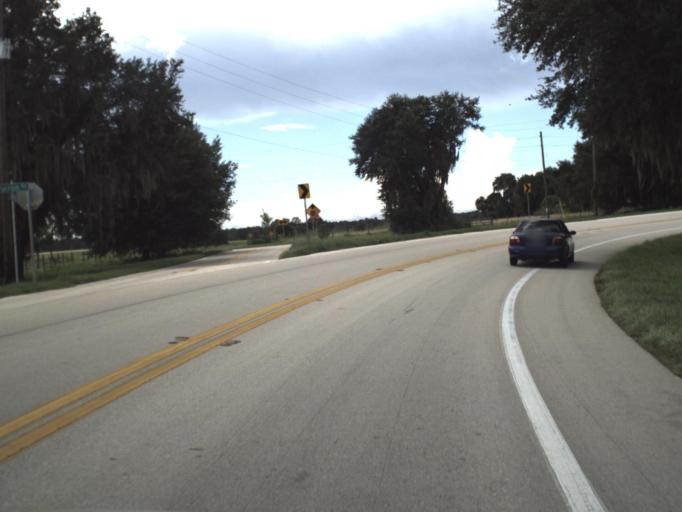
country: US
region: Florida
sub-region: Polk County
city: Fort Meade
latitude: 27.7482
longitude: -81.7636
